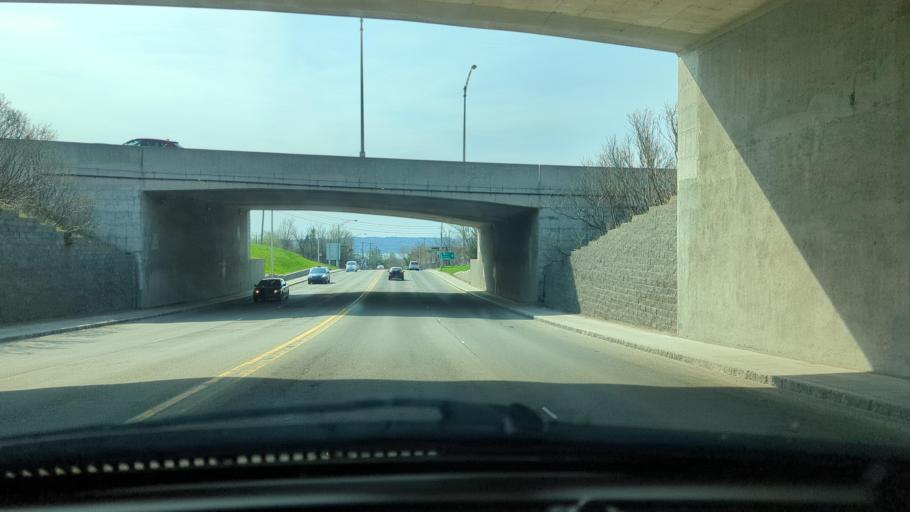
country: CA
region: Quebec
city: Quebec
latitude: 46.8567
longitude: -71.2181
